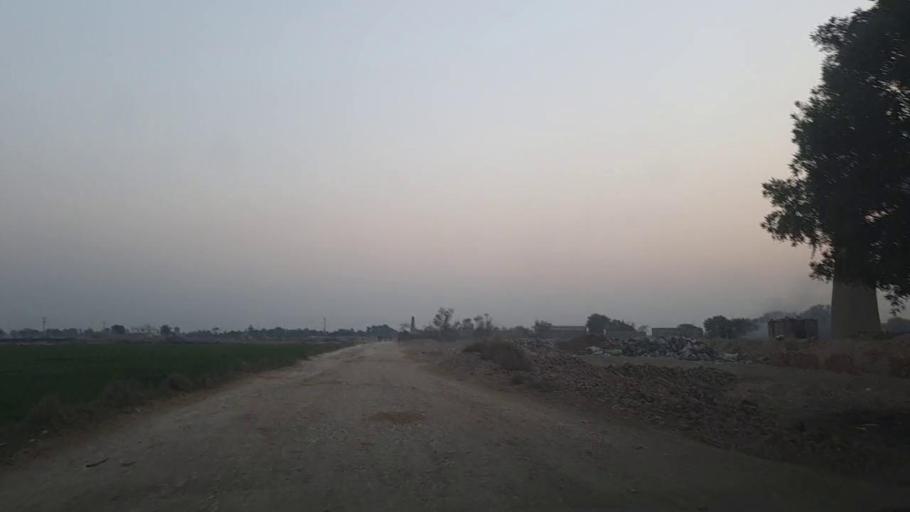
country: PK
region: Sindh
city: Naushahro Firoz
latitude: 26.8545
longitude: 68.0491
